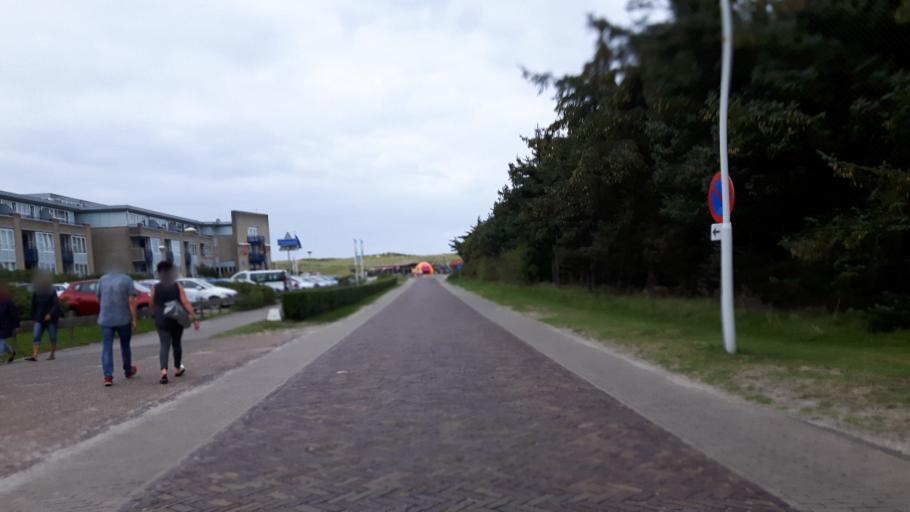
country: NL
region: Friesland
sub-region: Gemeente Ameland
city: Nes
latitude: 53.4565
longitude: 5.7777
